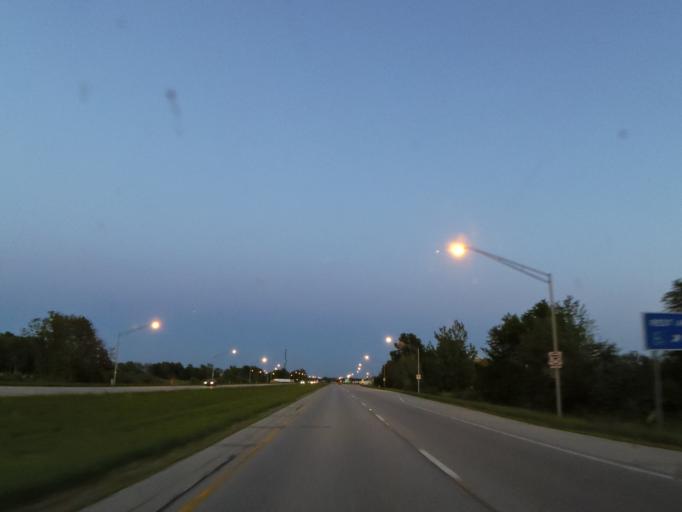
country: US
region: Indiana
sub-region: Hendricks County
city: Pittsboro
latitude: 39.9049
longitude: -86.5599
